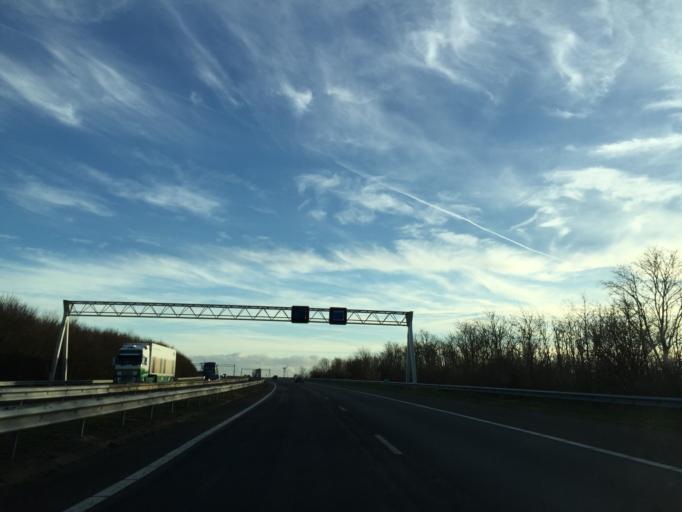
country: NL
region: North Brabant
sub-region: Gemeente Moerdijk
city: Willemstad
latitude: 51.7004
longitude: 4.3949
